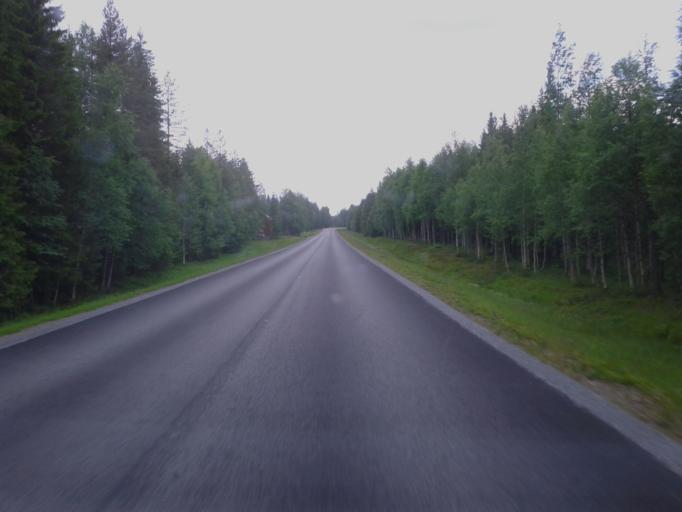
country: SE
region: Vaesterbotten
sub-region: Mala Kommun
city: Mala
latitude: 65.2000
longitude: 18.6989
